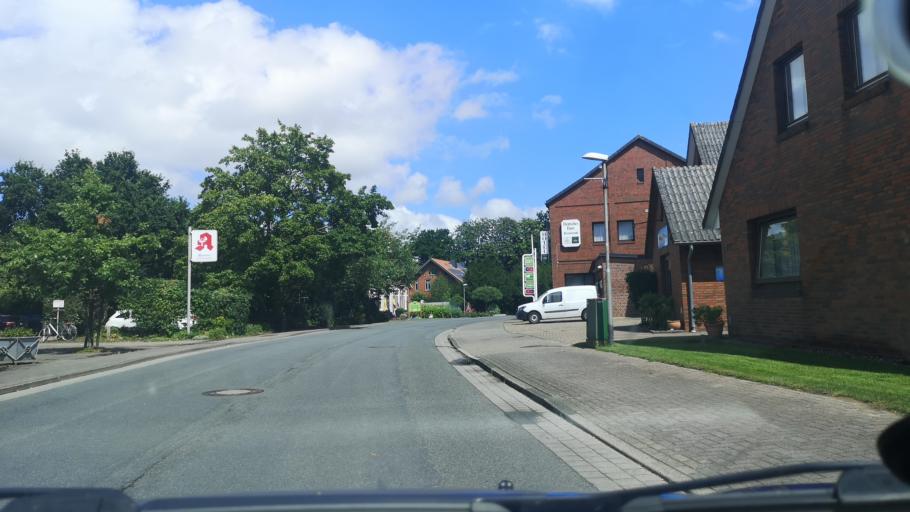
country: DE
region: Lower Saxony
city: Wremen
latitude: 53.6499
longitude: 8.5110
